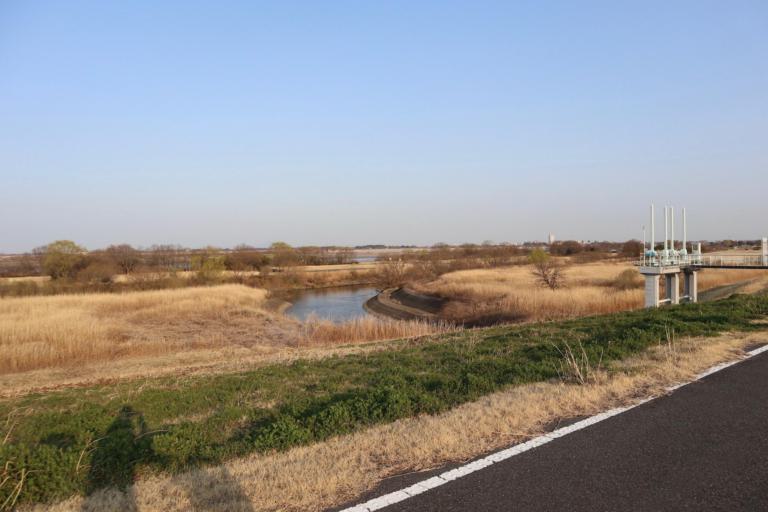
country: JP
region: Tochigi
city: Fujioka
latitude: 36.2146
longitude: 139.6600
